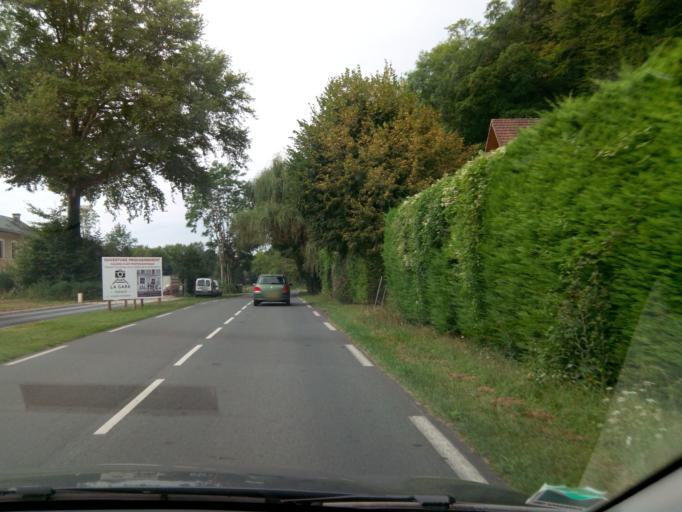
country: FR
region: Aquitaine
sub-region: Departement de la Dordogne
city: Eyvigues-et-Eybenes
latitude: 44.8704
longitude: 1.3626
